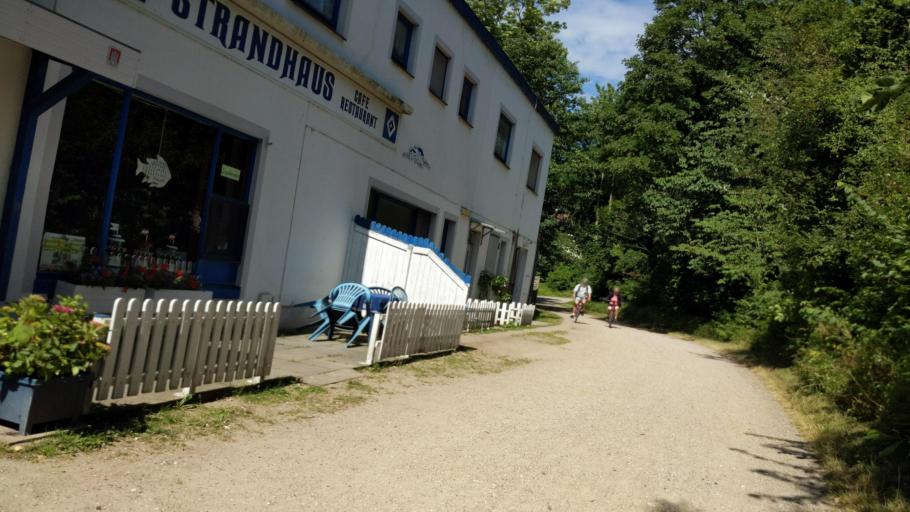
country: DE
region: Schleswig-Holstein
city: Ploen
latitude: 54.1547
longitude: 10.4463
